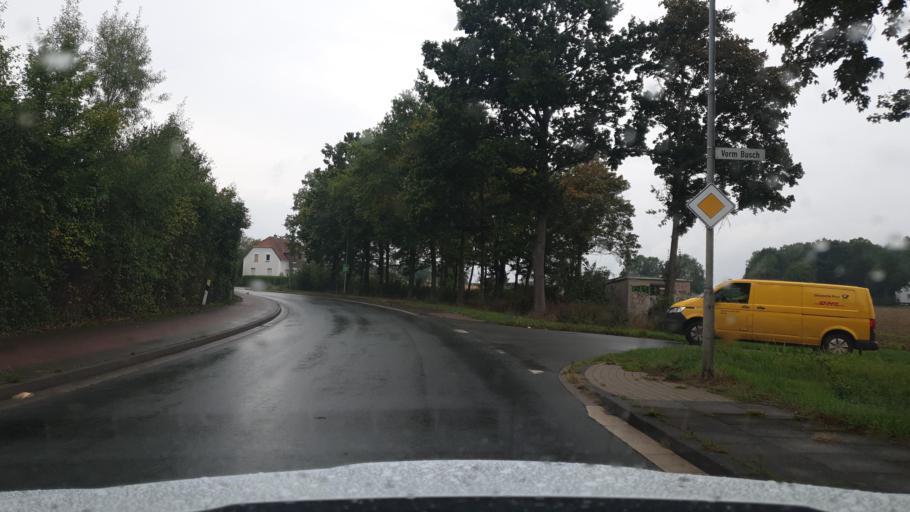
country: DE
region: North Rhine-Westphalia
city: Bad Oeynhausen
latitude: 52.2240
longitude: 8.7725
